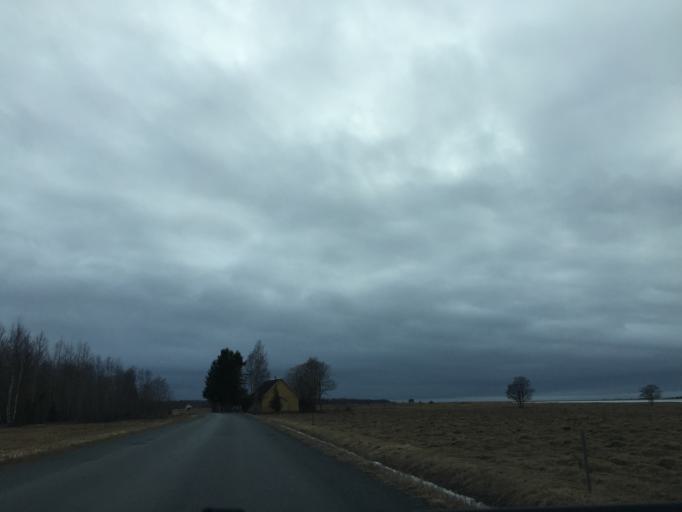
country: EE
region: Laeaene
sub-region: Haapsalu linn
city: Haapsalu
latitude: 58.8047
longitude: 23.5345
